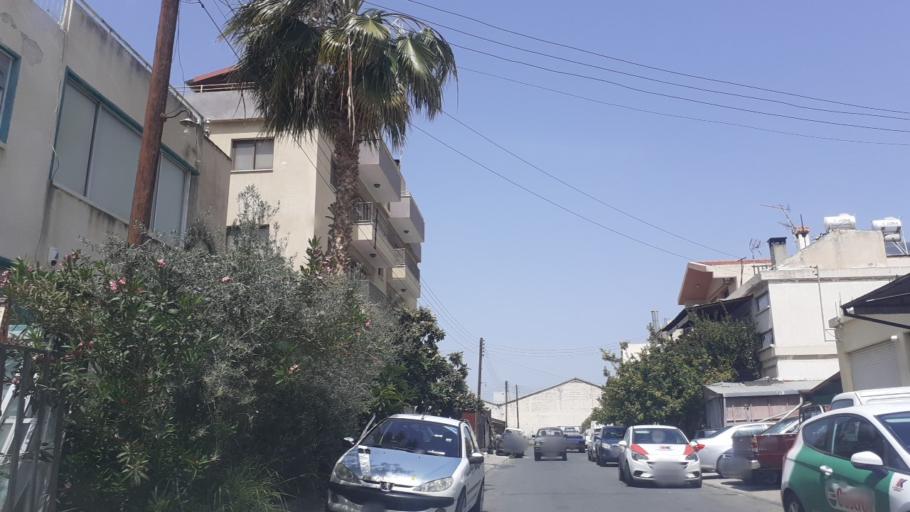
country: CY
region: Limassol
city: Limassol
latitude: 34.6698
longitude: 33.0175
